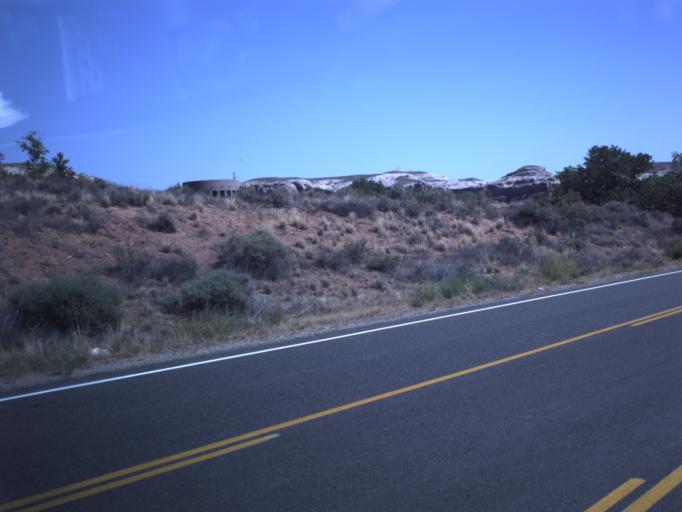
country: US
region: Utah
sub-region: San Juan County
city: Blanding
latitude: 37.2811
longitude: -109.5723
